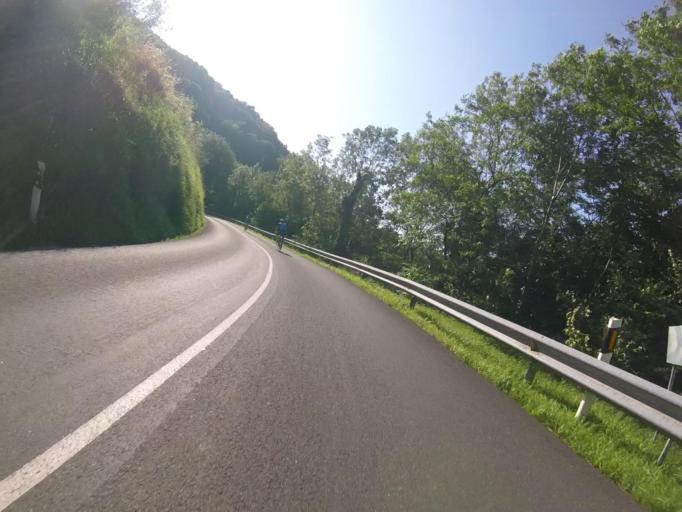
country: ES
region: Basque Country
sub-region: Provincia de Guipuzcoa
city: Asteasu
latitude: 43.2062
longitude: -2.1137
